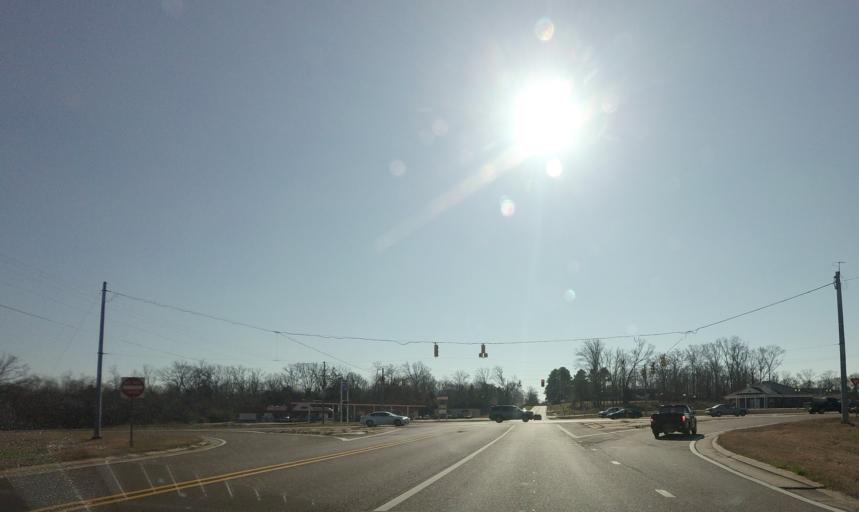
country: US
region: Tennessee
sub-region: Shelby County
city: Collierville
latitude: 34.9634
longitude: -89.6890
